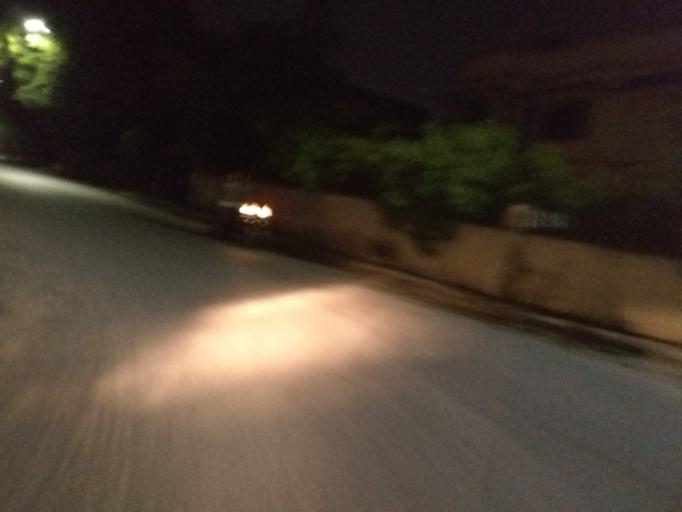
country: IN
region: Gujarat
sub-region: Ahmadabad
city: Ahmedabad
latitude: 23.0006
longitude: 72.5585
